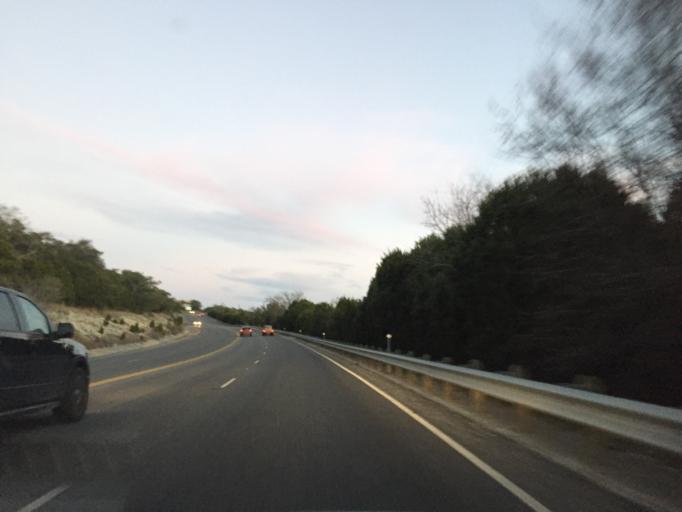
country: US
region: Texas
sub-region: Travis County
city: Jonestown
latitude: 30.5189
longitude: -97.8953
